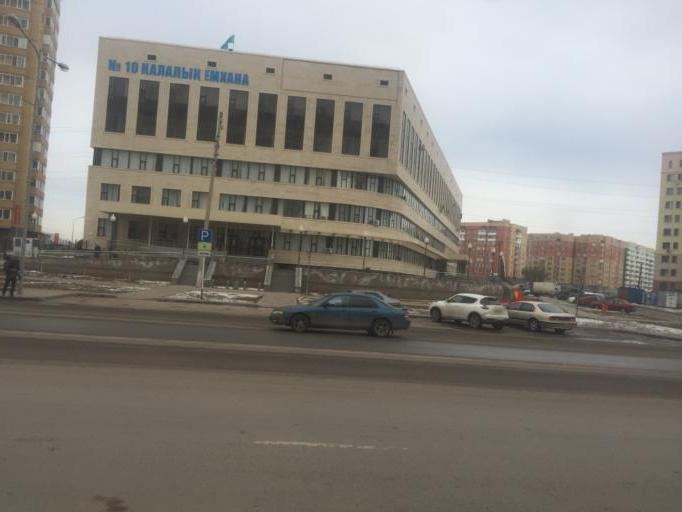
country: KZ
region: Astana Qalasy
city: Astana
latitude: 51.1684
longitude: 71.3914
